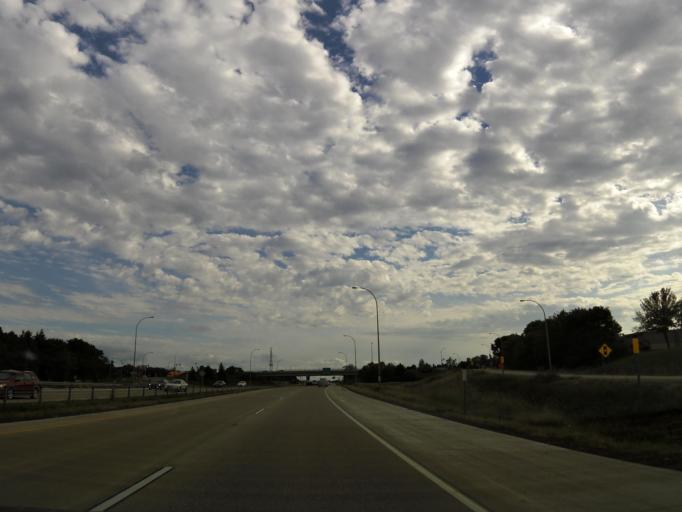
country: US
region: Minnesota
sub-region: Hennepin County
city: Edina
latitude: 44.8756
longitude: -93.3968
